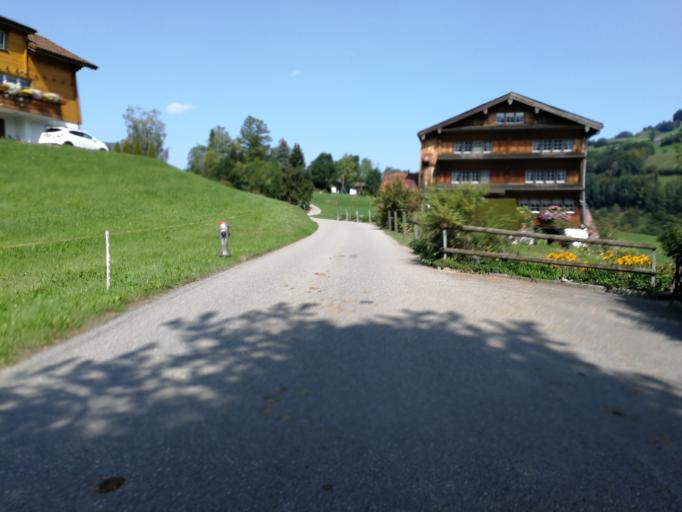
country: CH
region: Saint Gallen
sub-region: Wahlkreis Toggenburg
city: Krummenau
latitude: 47.2343
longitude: 9.1821
